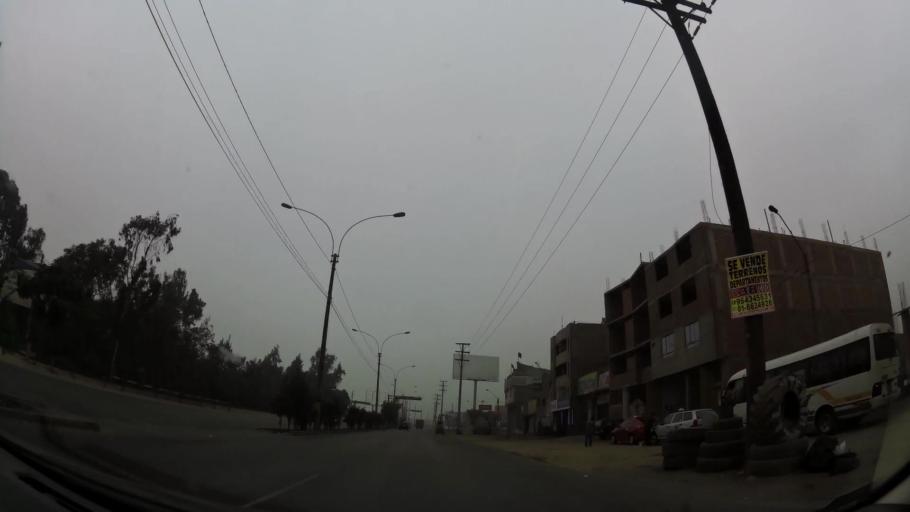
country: PE
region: Lima
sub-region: Lima
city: Santa Maria
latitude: -11.9975
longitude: -76.8358
